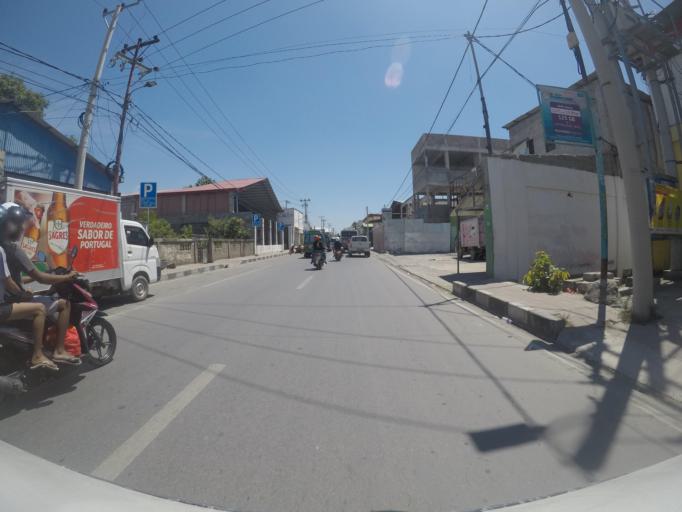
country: TL
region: Dili
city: Dili
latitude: -8.5549
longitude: 125.5896
